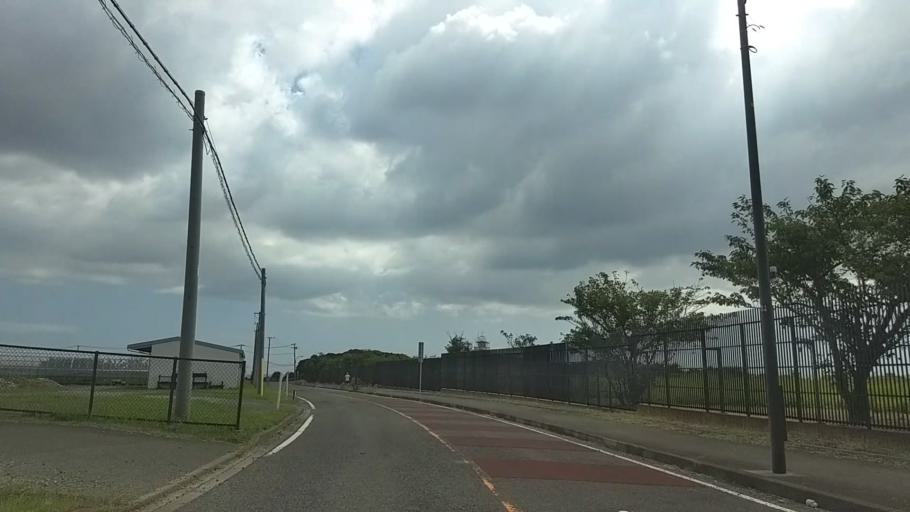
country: JP
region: Kanagawa
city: Miura
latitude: 35.1950
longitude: 139.6149
